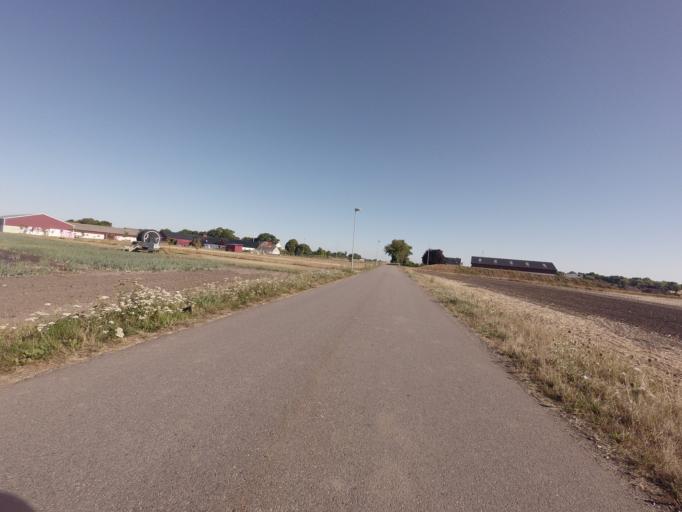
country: SE
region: Skane
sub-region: Trelleborgs Kommun
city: Trelleborg
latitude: 55.3900
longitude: 13.1113
